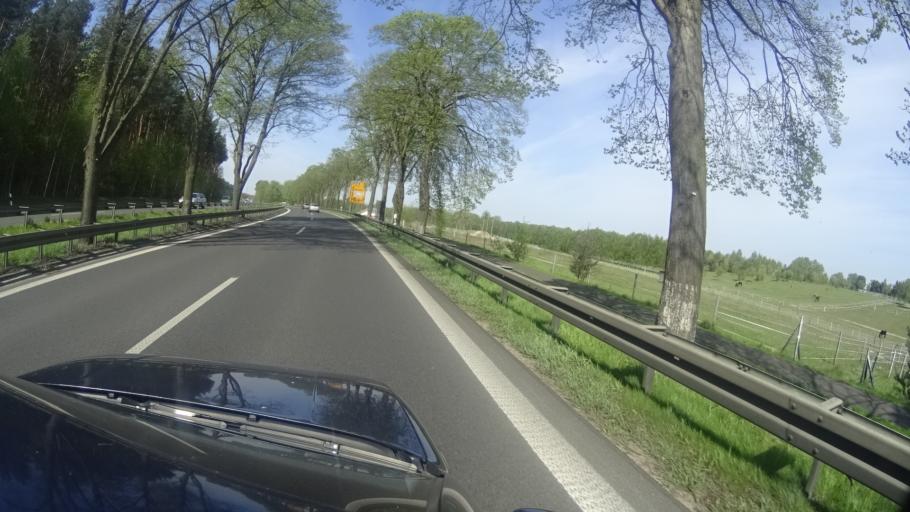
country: DE
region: Brandenburg
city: Dallgow-Doeberitz
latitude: 52.5349
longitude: 13.0743
